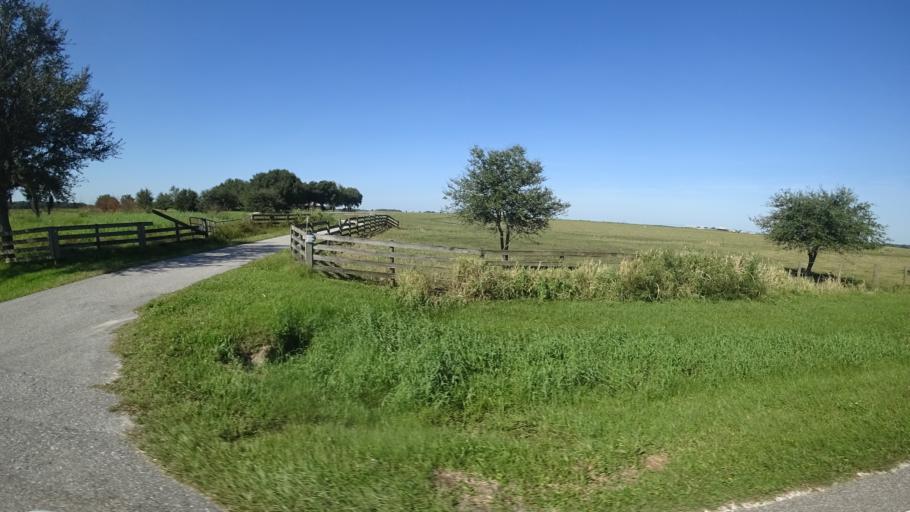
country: US
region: Florida
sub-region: Sarasota County
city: Lake Sarasota
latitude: 27.3627
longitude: -82.2684
